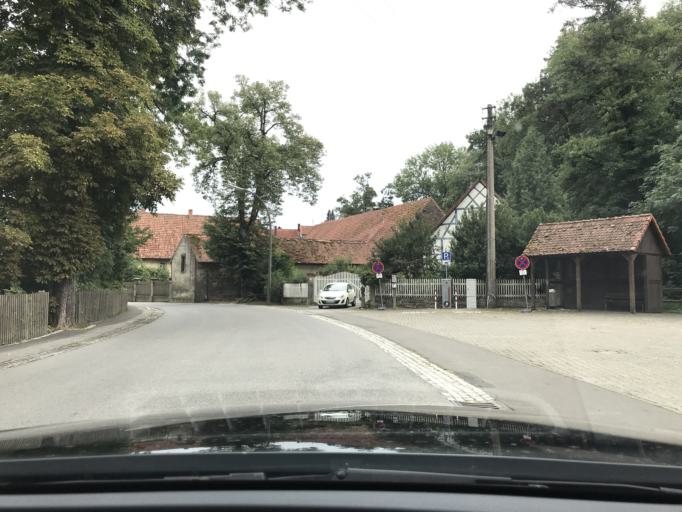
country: DE
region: Bavaria
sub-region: Regierungsbezirk Unterfranken
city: Burgpreppach
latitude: 50.1406
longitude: 10.6508
